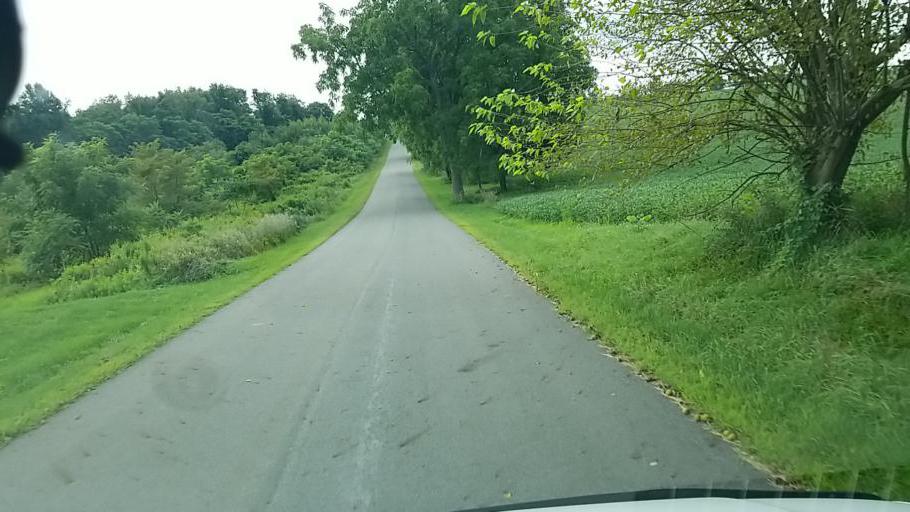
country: US
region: Pennsylvania
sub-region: Dauphin County
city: Elizabethville
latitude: 40.5184
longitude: -76.8846
